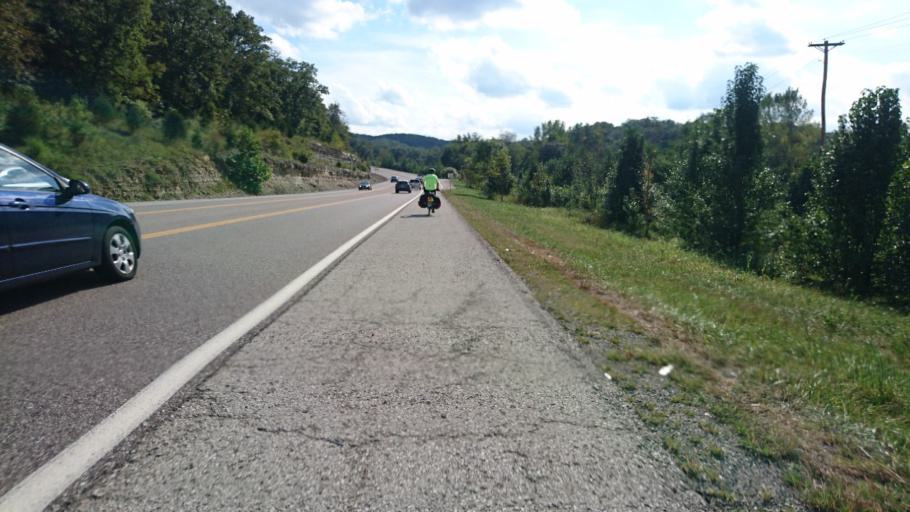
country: US
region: Missouri
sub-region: Saint Louis County
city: Eureka
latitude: 38.5426
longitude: -90.6304
